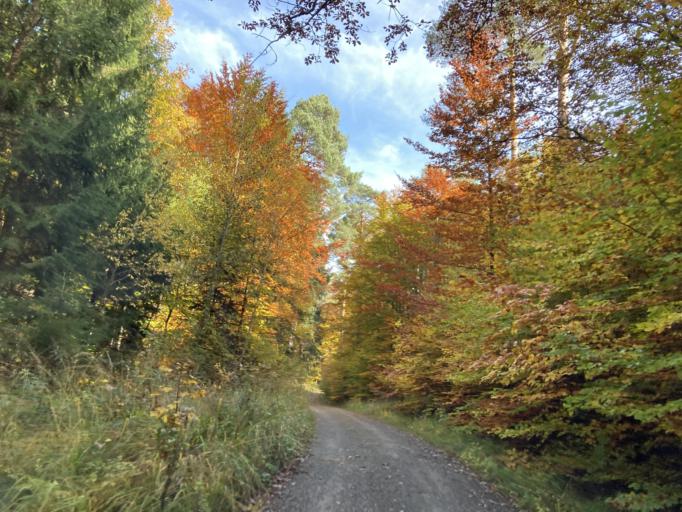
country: DE
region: Baden-Wuerttemberg
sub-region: Tuebingen Region
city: Rottenburg
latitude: 48.4631
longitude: 8.9785
